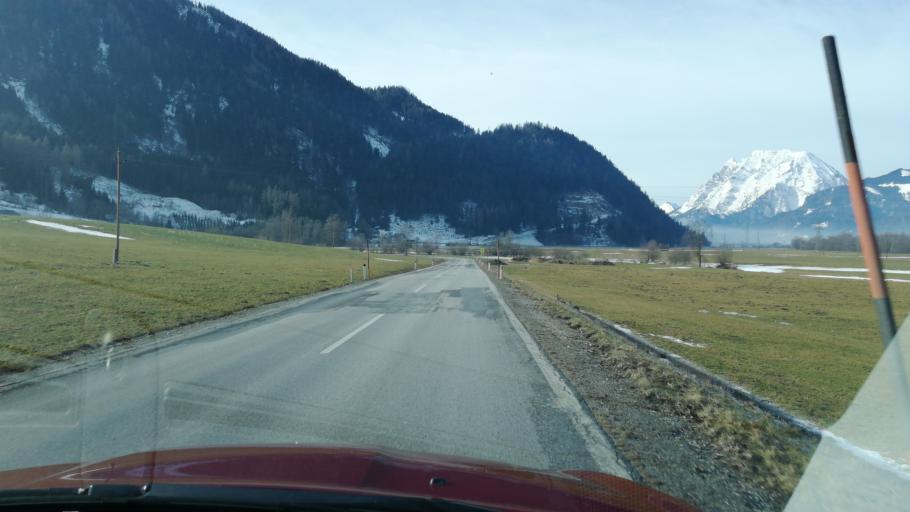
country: AT
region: Styria
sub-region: Politischer Bezirk Liezen
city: Weissenbach bei Liezen
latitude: 47.5459
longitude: 14.1913
